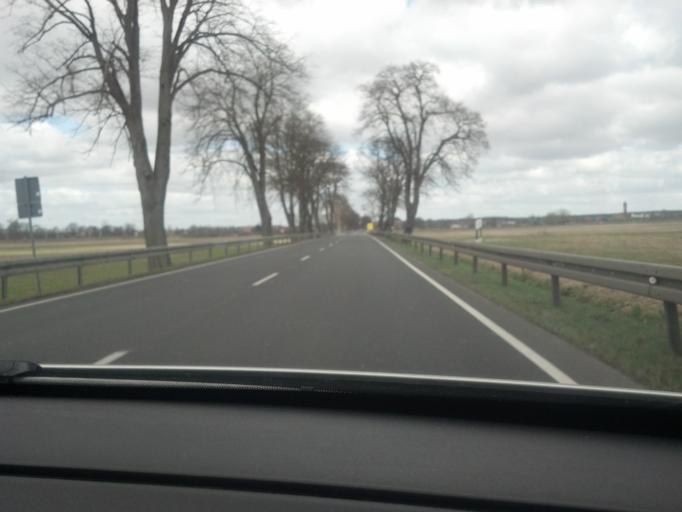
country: DE
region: Mecklenburg-Vorpommern
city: Neustrelitz
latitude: 53.3161
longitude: 13.0993
